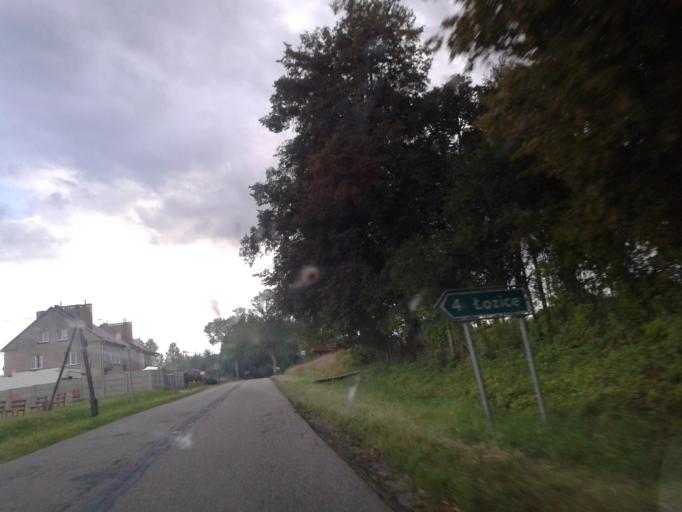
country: PL
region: West Pomeranian Voivodeship
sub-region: Powiat koszalinski
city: Bobolice
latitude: 53.9050
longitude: 16.5426
